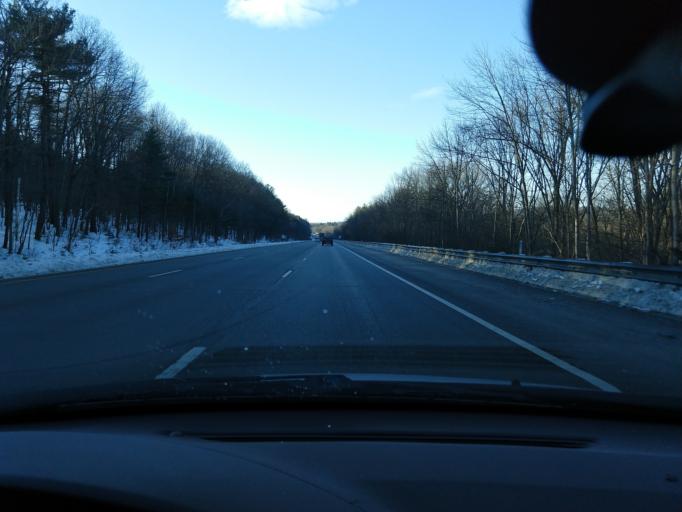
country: US
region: Massachusetts
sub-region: Worcester County
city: Harvard
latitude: 42.5031
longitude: -71.5299
